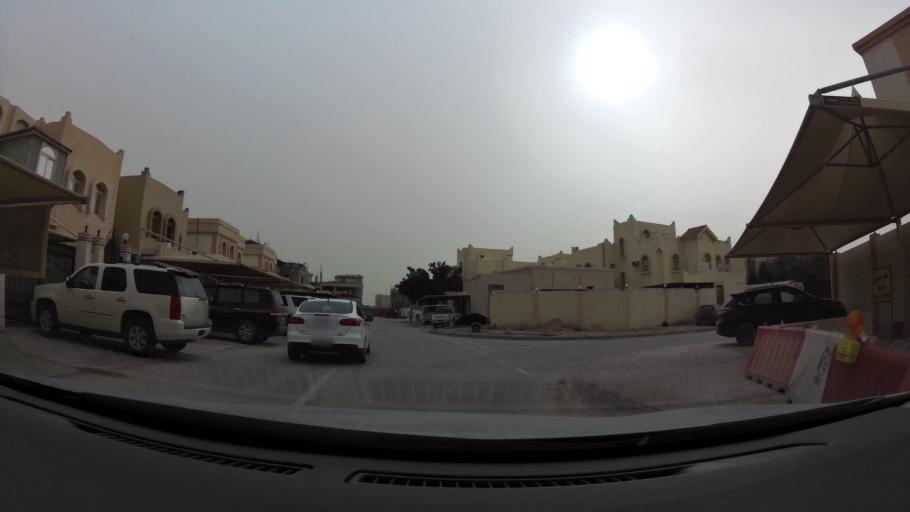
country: QA
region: Baladiyat ad Dawhah
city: Doha
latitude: 25.2439
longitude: 51.5007
